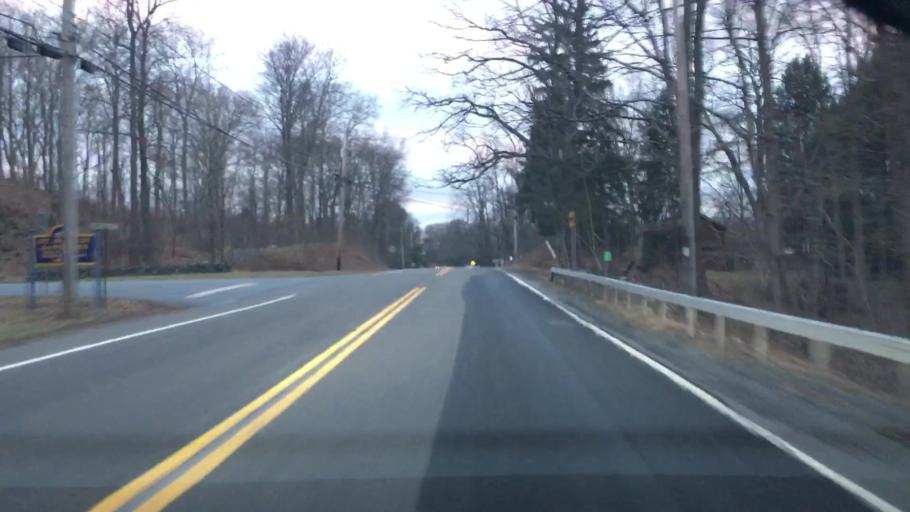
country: US
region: New York
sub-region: Dutchess County
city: Red Oaks Mill
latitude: 41.6671
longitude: -73.8787
